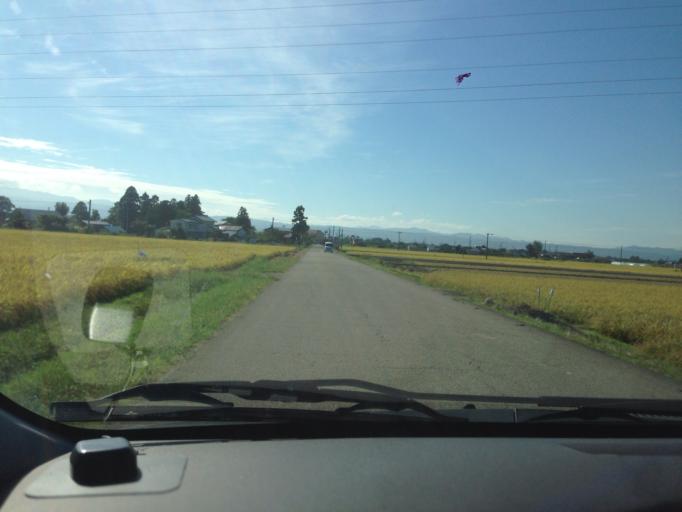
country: JP
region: Fukushima
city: Kitakata
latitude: 37.5384
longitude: 139.9211
